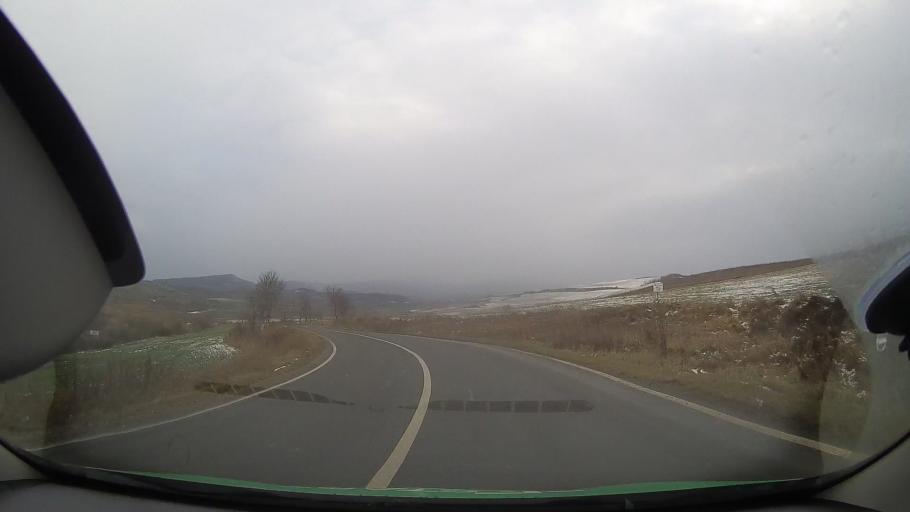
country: RO
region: Sibiu
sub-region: Comuna Blajel
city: Blajel
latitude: 46.2396
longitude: 24.3027
